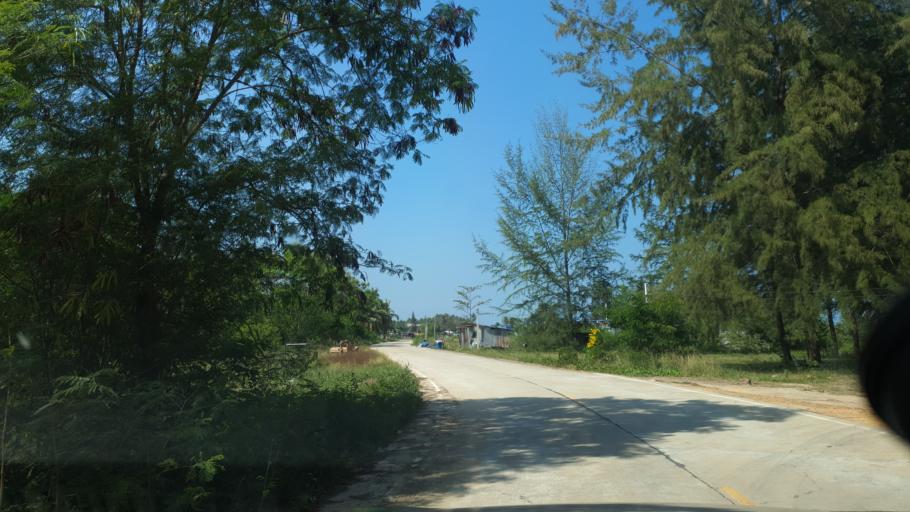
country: TH
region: Surat Thani
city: Tha Chana
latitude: 9.5995
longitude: 99.2093
